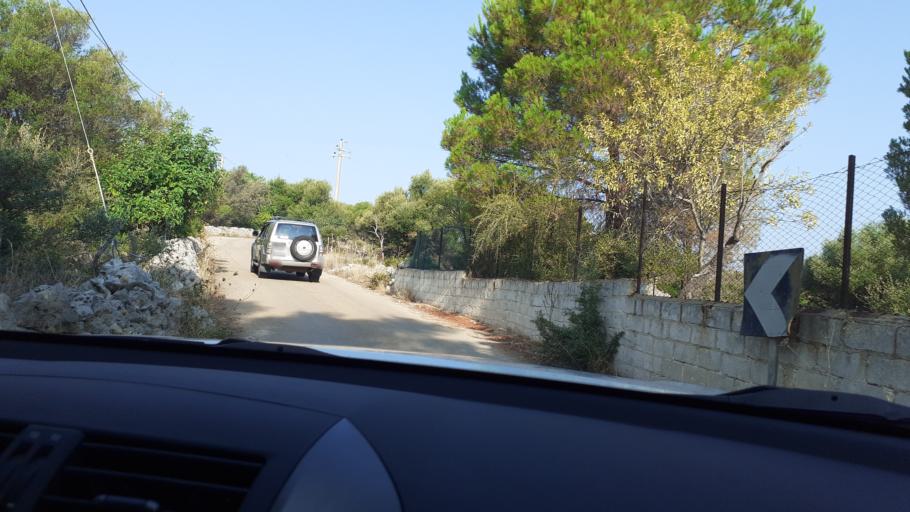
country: IT
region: Sicily
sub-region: Provincia di Siracusa
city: Cassibile
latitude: 36.9767
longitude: 15.1559
